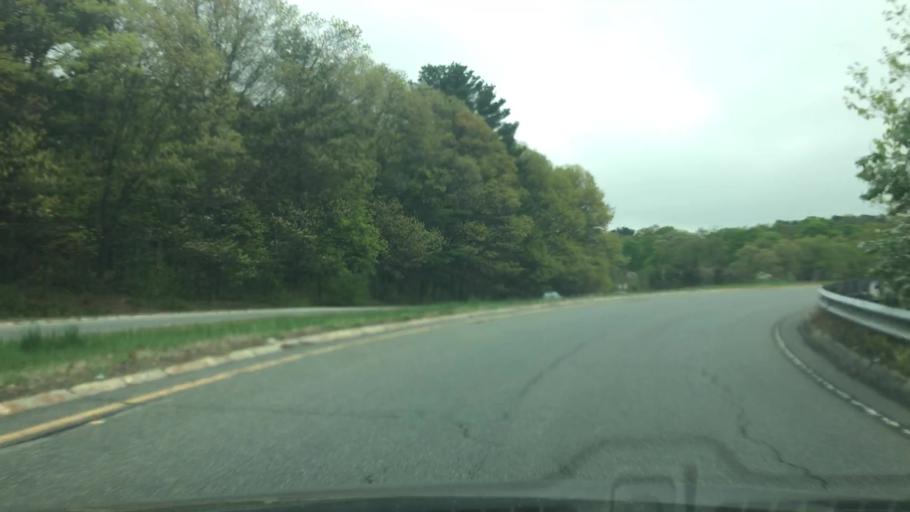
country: US
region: Massachusetts
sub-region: Essex County
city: Lynnfield
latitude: 42.5152
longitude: -71.0271
